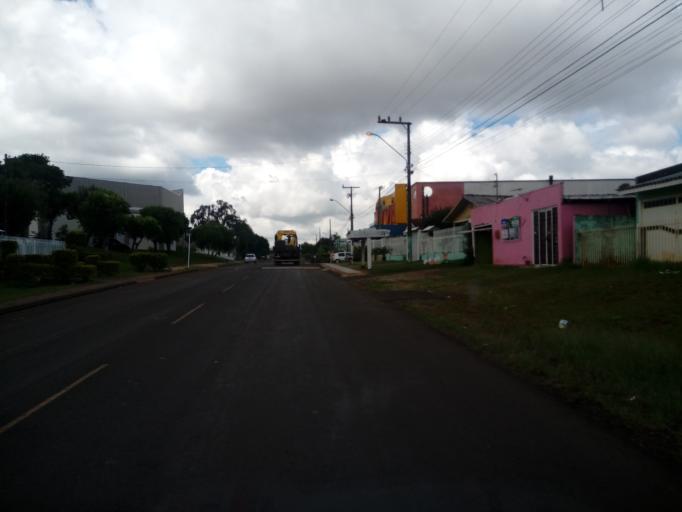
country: BR
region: Santa Catarina
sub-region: Chapeco
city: Chapeco
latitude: -27.0830
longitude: -52.6079
